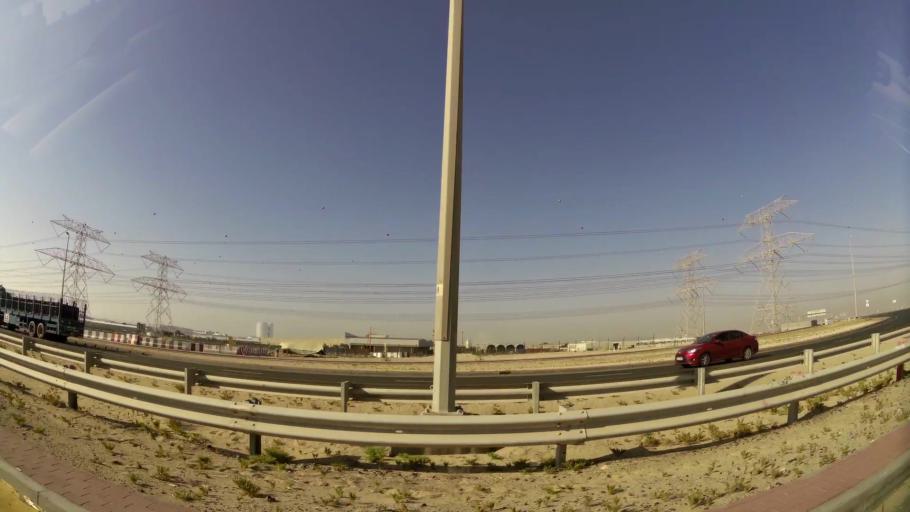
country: AE
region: Dubai
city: Dubai
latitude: 24.9376
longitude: 55.0751
